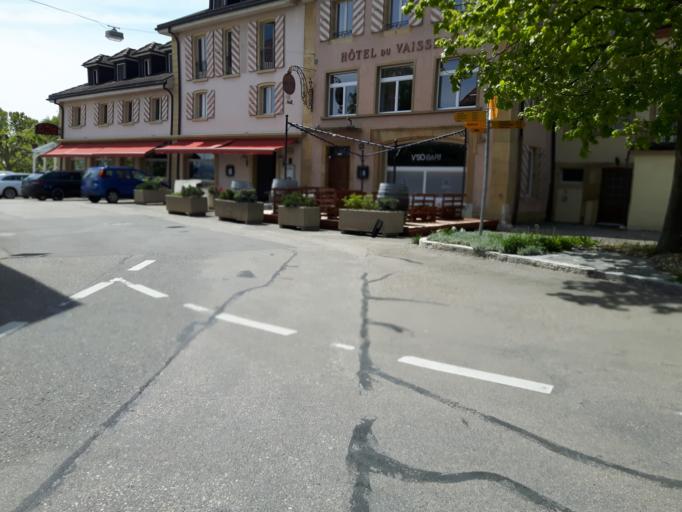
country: CH
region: Neuchatel
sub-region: Boudry District
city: Cortaillod
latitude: 46.9407
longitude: 6.8525
